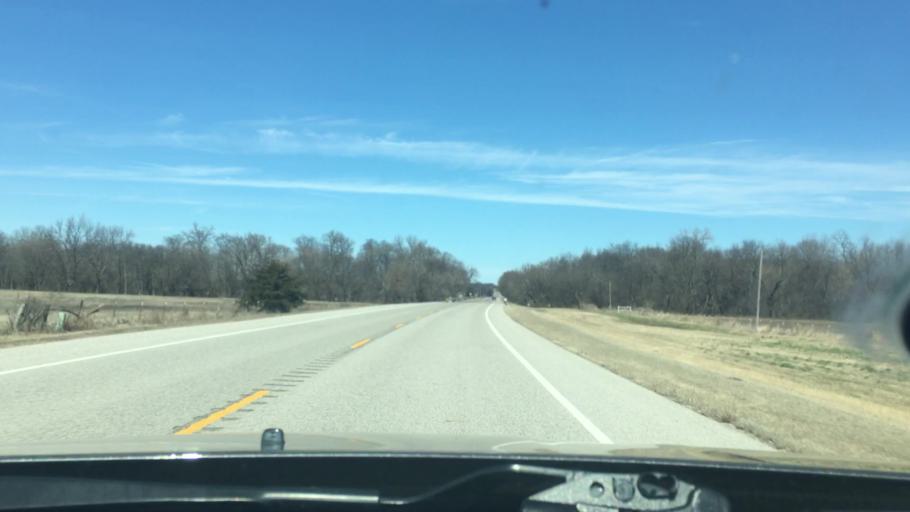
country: US
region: Oklahoma
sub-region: Murray County
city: Sulphur
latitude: 34.3880
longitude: -96.9510
